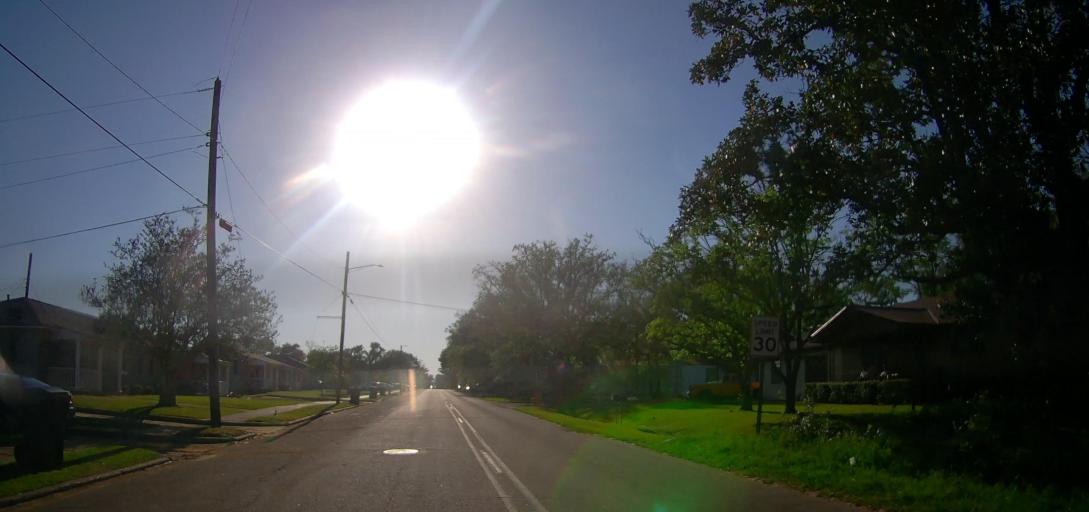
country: US
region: Georgia
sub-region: Ben Hill County
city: Fitzgerald
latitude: 31.7059
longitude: -83.2460
